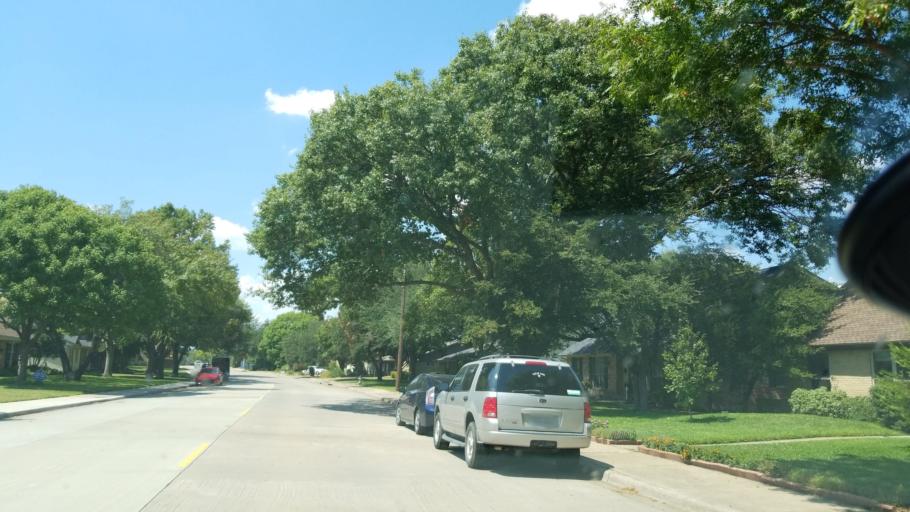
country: US
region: Texas
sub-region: Dallas County
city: Richardson
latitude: 32.8924
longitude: -96.7156
